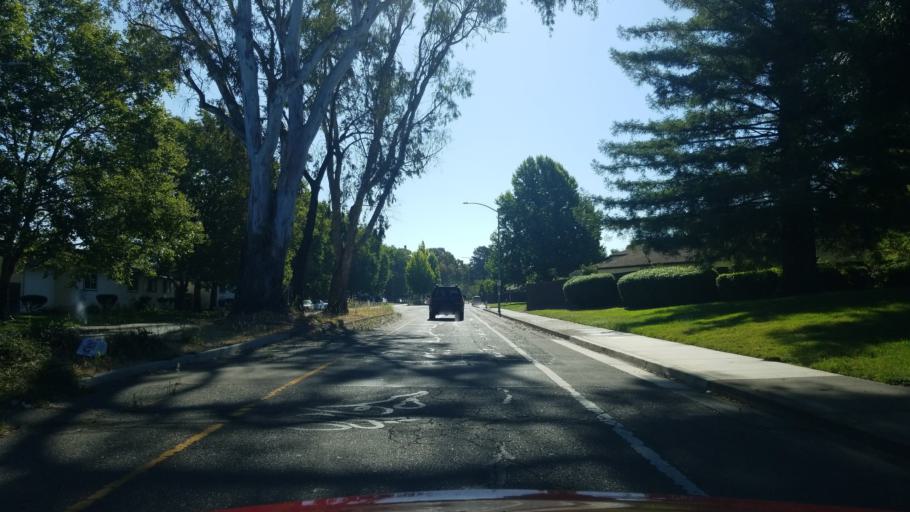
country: US
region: California
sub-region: Sonoma County
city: Roseland
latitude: 38.4413
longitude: -122.7433
